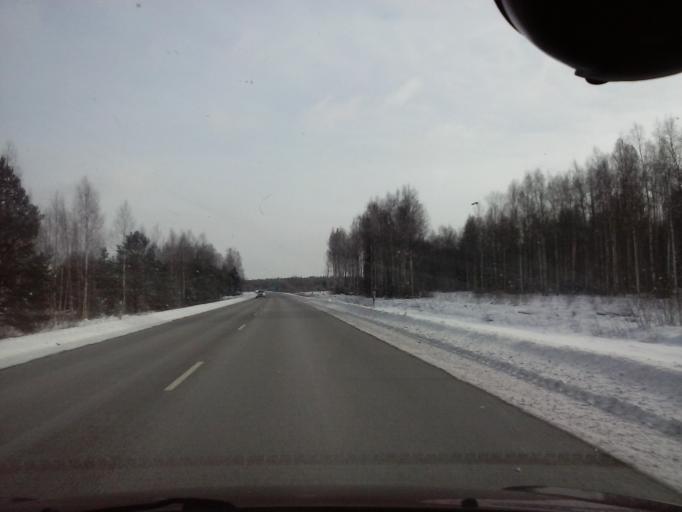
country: EE
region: Paernumaa
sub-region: Saarde vald
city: Kilingi-Nomme
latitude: 58.1743
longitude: 24.8072
